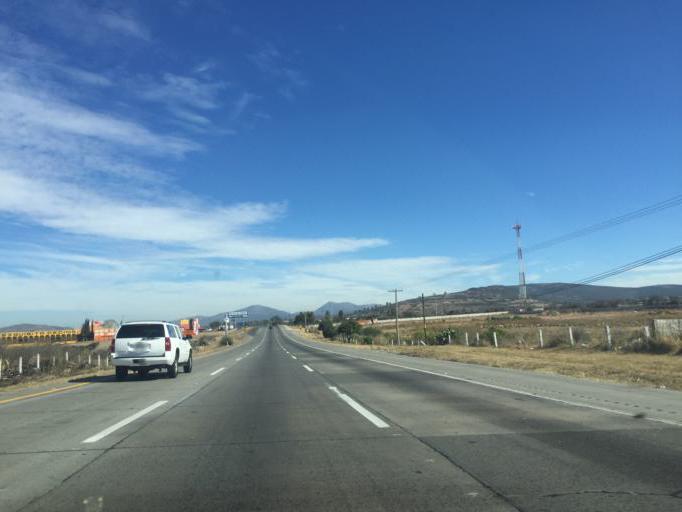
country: MX
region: Queretaro
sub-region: San Juan del Rio
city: Paso de Mata
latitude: 20.3099
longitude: -99.9332
